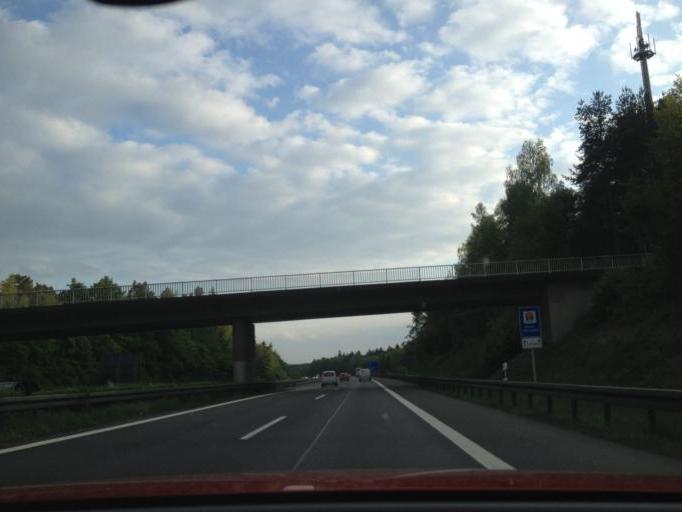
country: DE
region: Bavaria
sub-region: Upper Palatinate
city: Weiden
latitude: 49.7088
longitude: 12.1413
